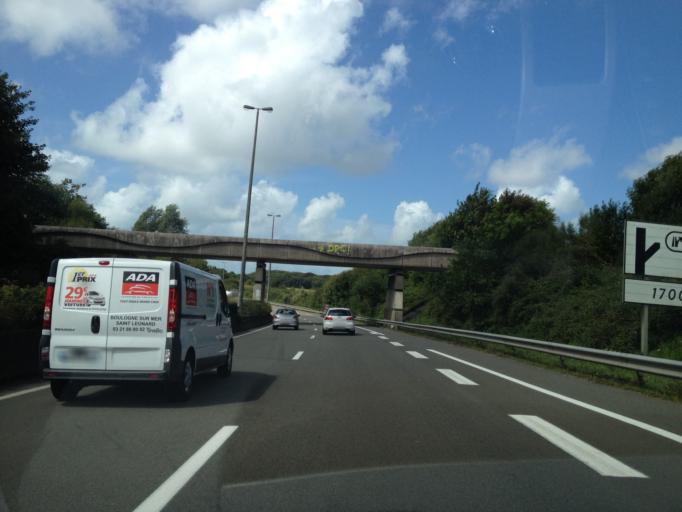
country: FR
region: Nord-Pas-de-Calais
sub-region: Departement du Pas-de-Calais
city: Saint-Martin-Boulogne
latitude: 50.7330
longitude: 1.6462
